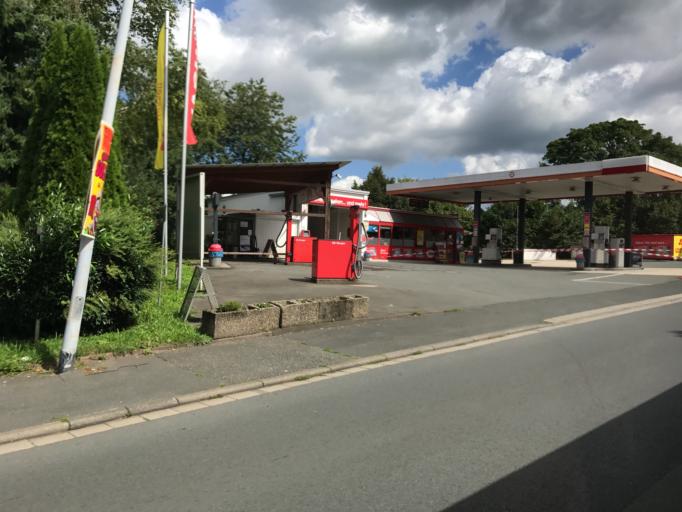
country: DE
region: Hesse
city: Weilburg
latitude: 50.4809
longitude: 8.2793
